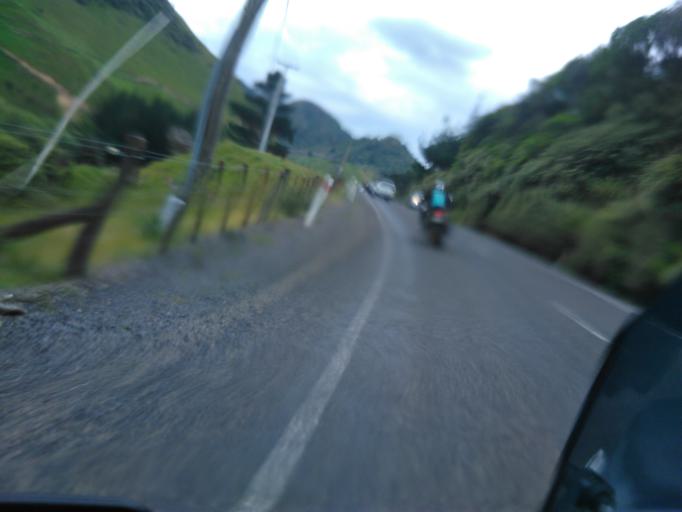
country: NZ
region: Bay of Plenty
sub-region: Opotiki District
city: Opotiki
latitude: -38.3712
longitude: 177.4876
